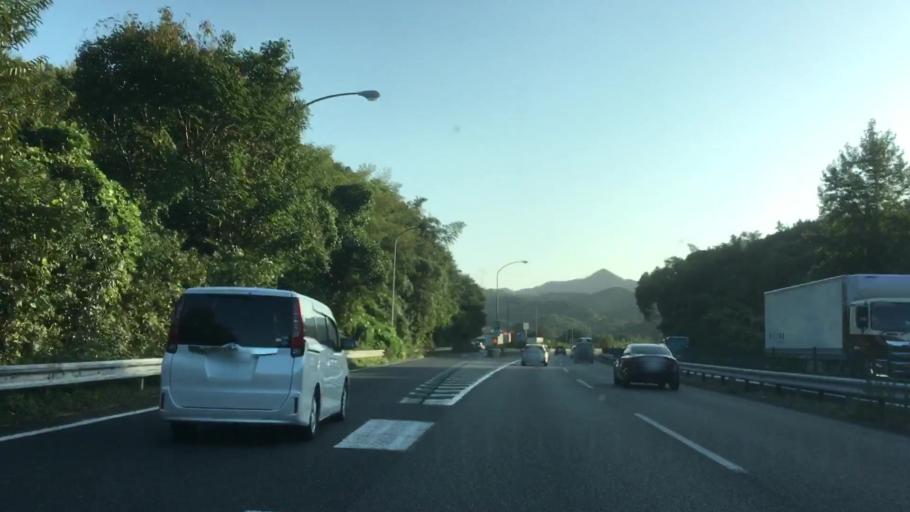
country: JP
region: Yamaguchi
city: Shimonoseki
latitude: 34.0527
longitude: 131.0059
